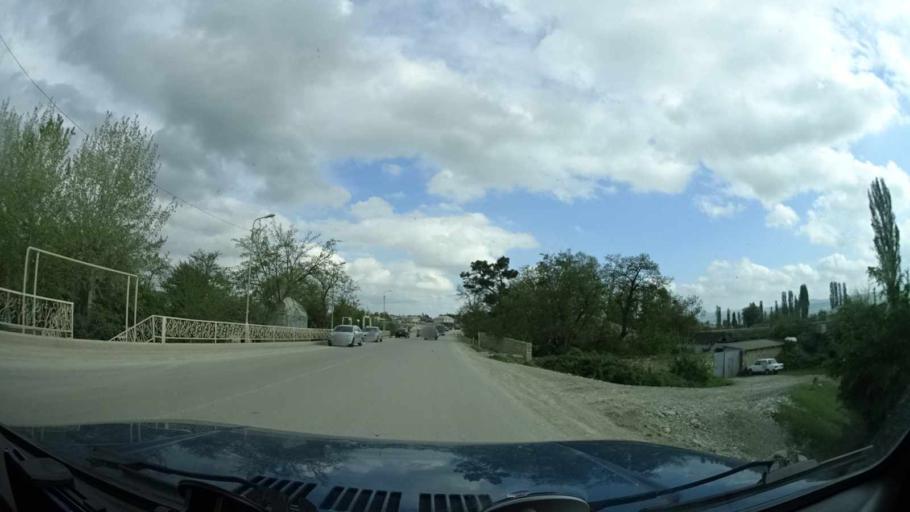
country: AZ
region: Samaxi
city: Shamakhi
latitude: 40.5943
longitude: 48.7023
